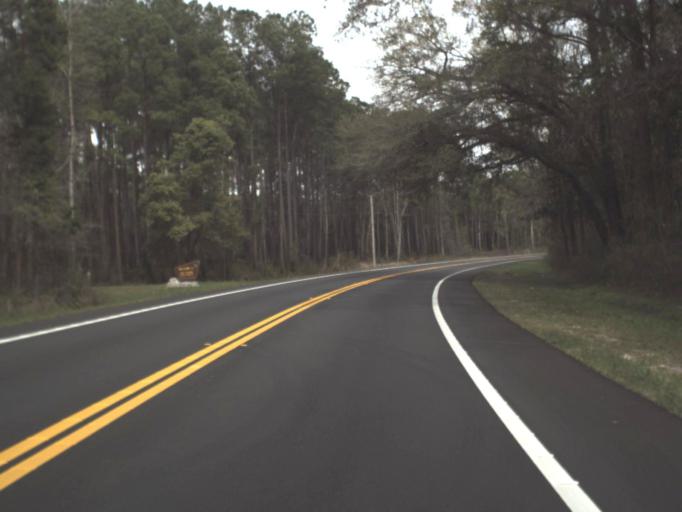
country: US
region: Florida
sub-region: Gadsden County
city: Quincy
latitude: 30.3878
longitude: -84.6425
